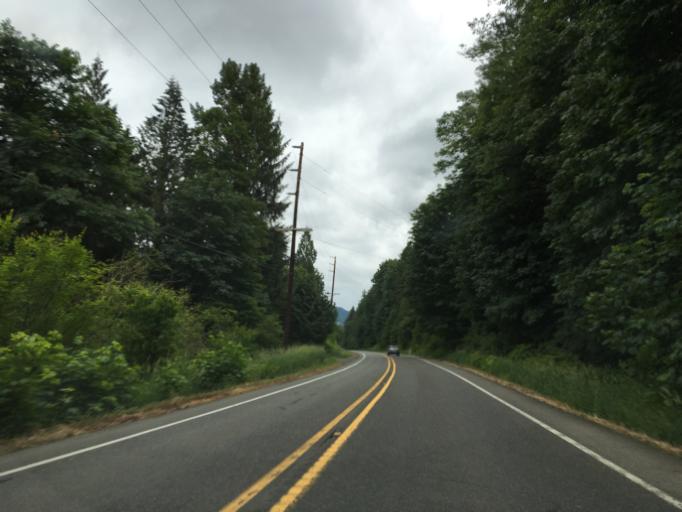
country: US
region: Washington
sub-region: Whatcom County
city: Peaceful Valley
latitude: 48.8727
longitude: -122.1565
